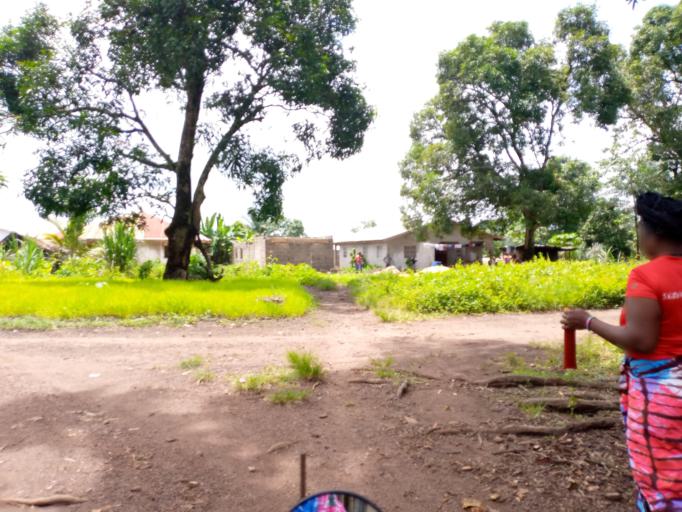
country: SL
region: Northern Province
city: Magburaka
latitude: 8.7269
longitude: -11.9272
